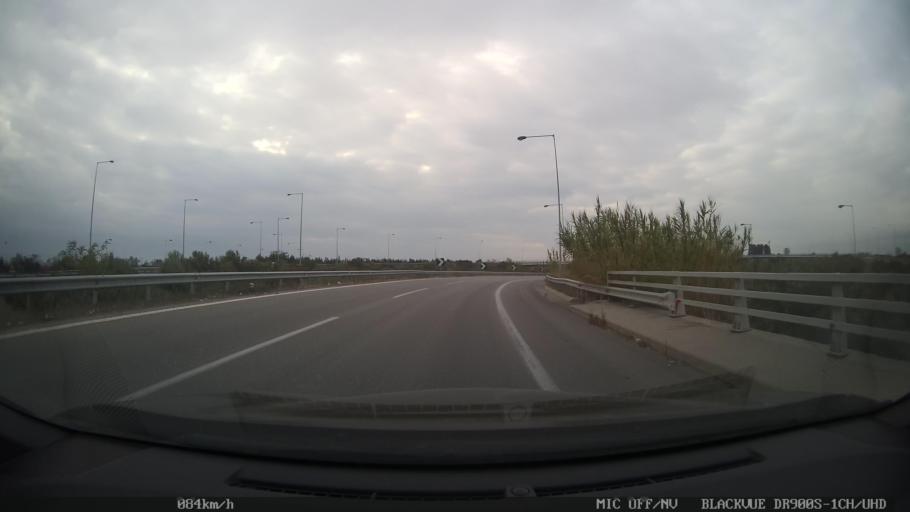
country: GR
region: Central Macedonia
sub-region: Nomos Thessalonikis
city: Kalochori
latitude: 40.6558
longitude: 22.8417
